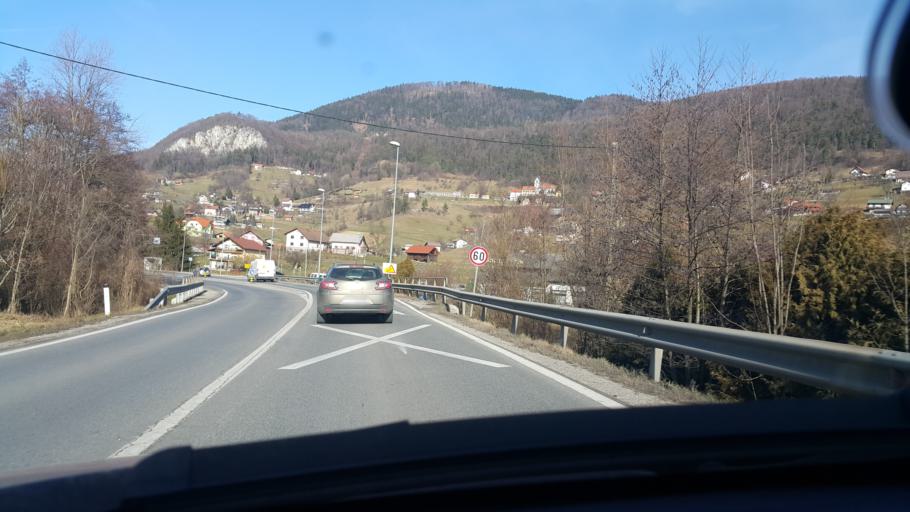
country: SI
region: Dobrna
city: Dobrna
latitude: 46.3402
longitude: 15.1728
